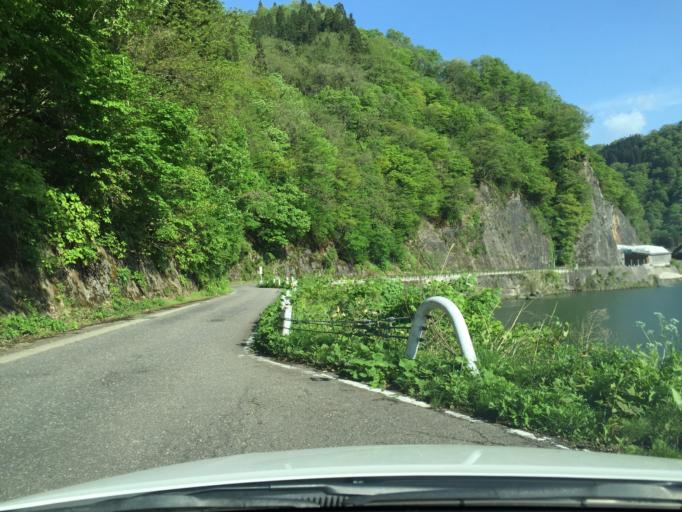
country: JP
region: Fukushima
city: Kitakata
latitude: 37.6649
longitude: 139.5918
